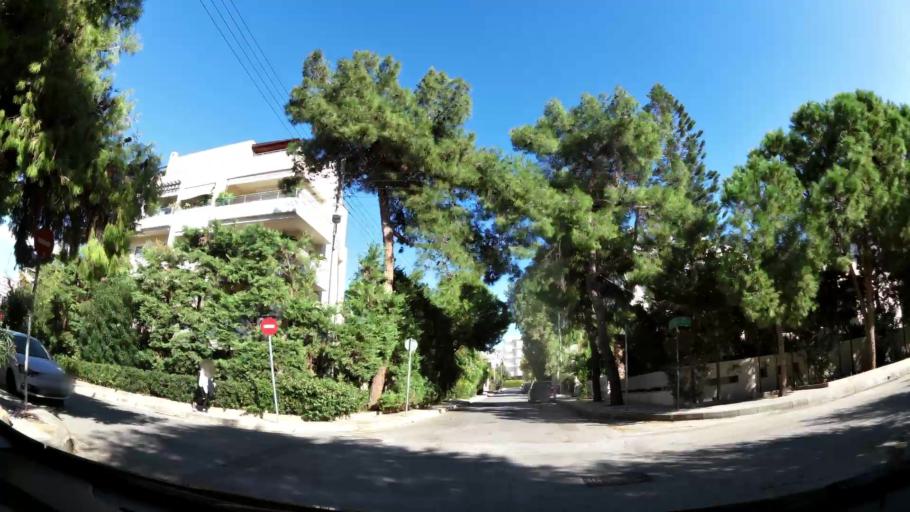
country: GR
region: Attica
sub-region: Nomarchia Athinas
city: Glyfada
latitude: 37.8531
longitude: 23.7596
